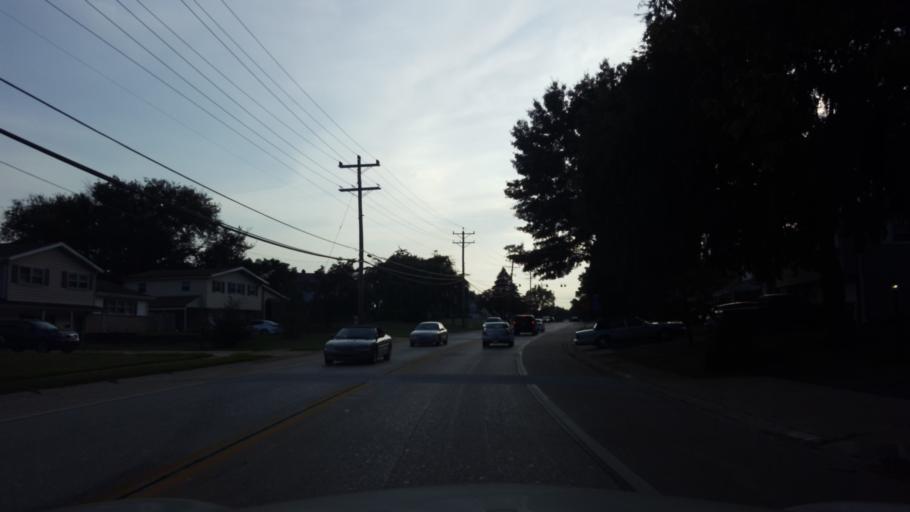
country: US
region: Delaware
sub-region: New Castle County
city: Pike Creek Valley
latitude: 39.7328
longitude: -75.6600
